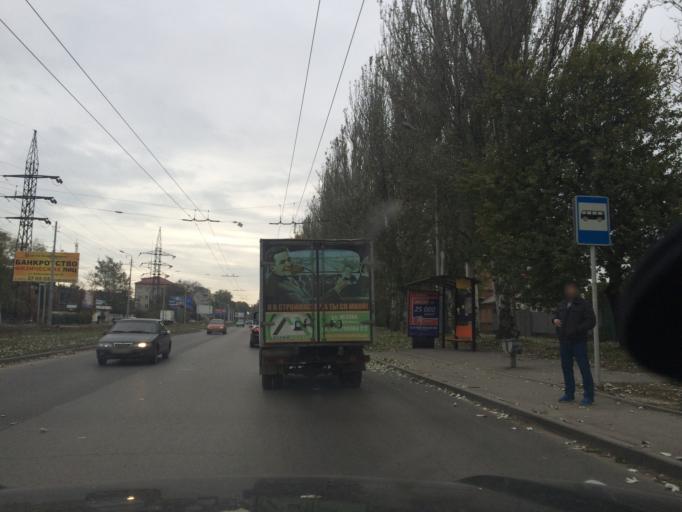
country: RU
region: Rostov
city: Taganrog
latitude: 47.2455
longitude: 38.9177
